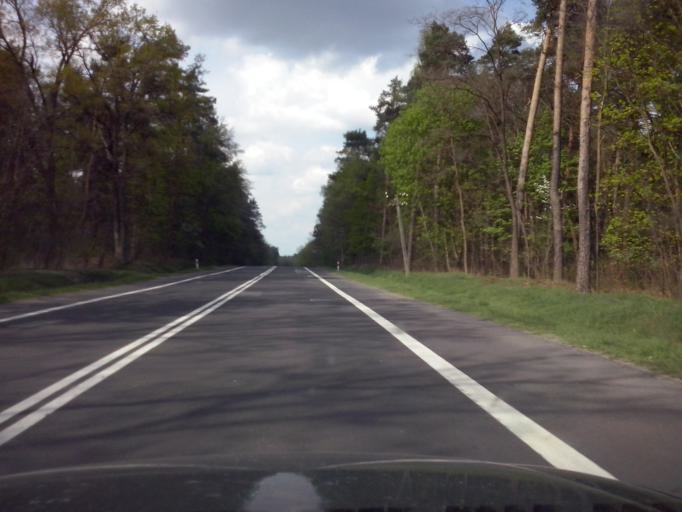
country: PL
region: Subcarpathian Voivodeship
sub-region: Powiat rzeszowski
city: Gorno
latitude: 50.2642
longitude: 22.1404
